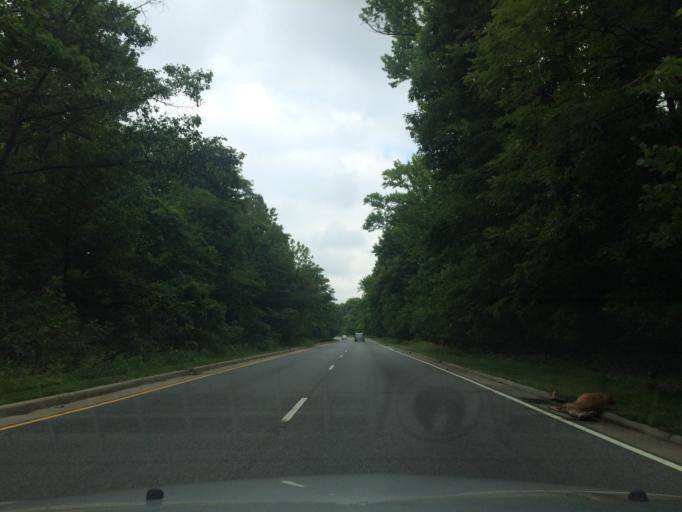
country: US
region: Maryland
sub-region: Prince George's County
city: Silver Hill
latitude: 38.8490
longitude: -76.9433
